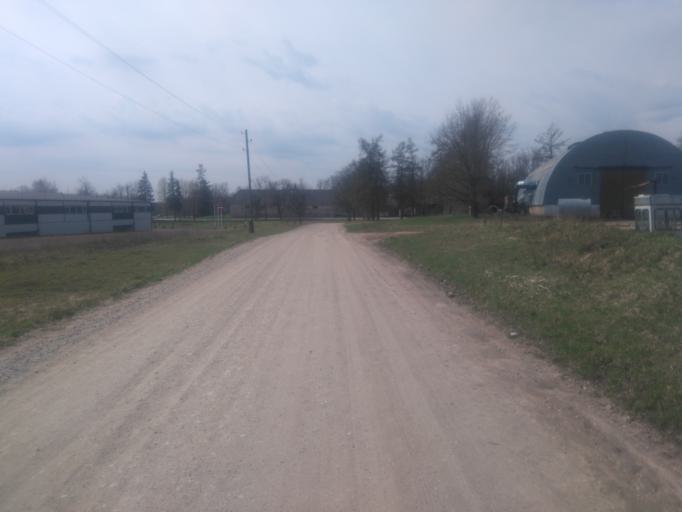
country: LV
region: Vecpiebalga
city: Vecpiebalga
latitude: 57.0206
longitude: 25.8351
